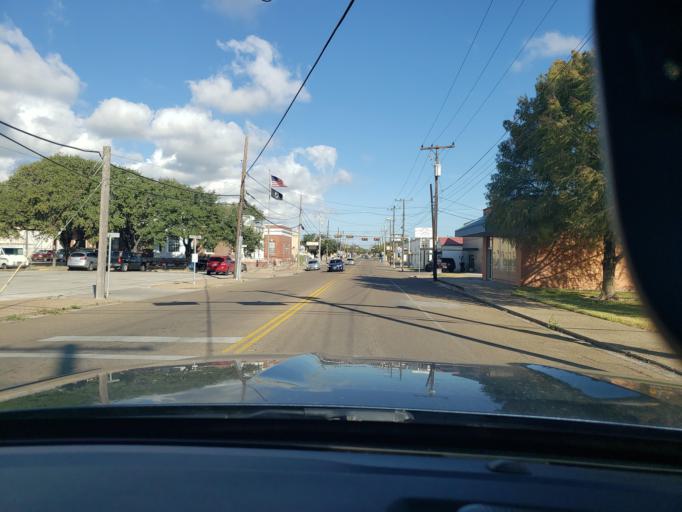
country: US
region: Texas
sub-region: Bee County
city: Beeville
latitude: 28.4021
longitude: -97.7482
